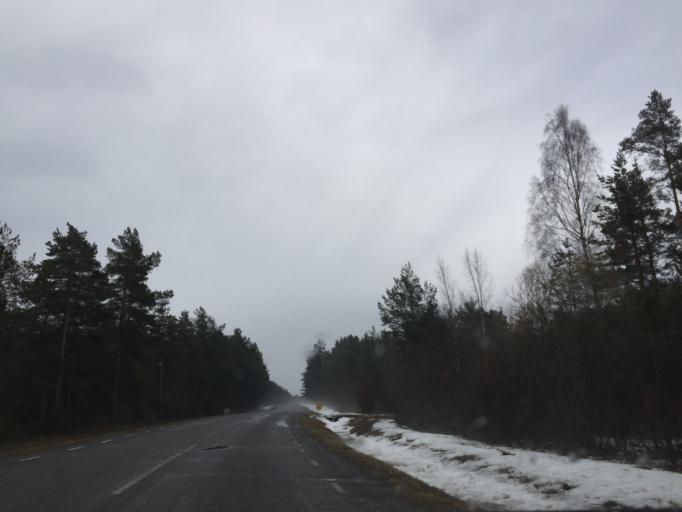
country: EE
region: Saare
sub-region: Orissaare vald
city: Orissaare
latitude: 58.6064
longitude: 22.9676
